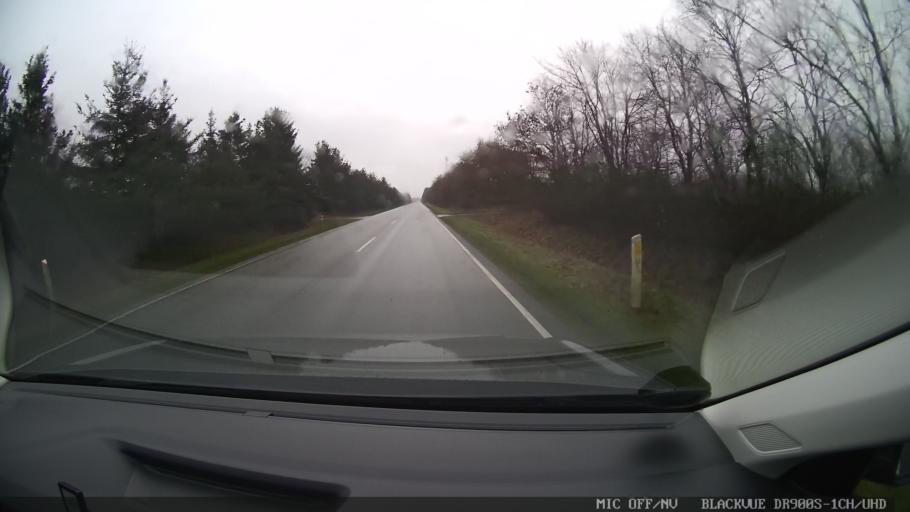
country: DK
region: Central Jutland
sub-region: Herning Kommune
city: Avlum
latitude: 56.2915
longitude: 8.9116
